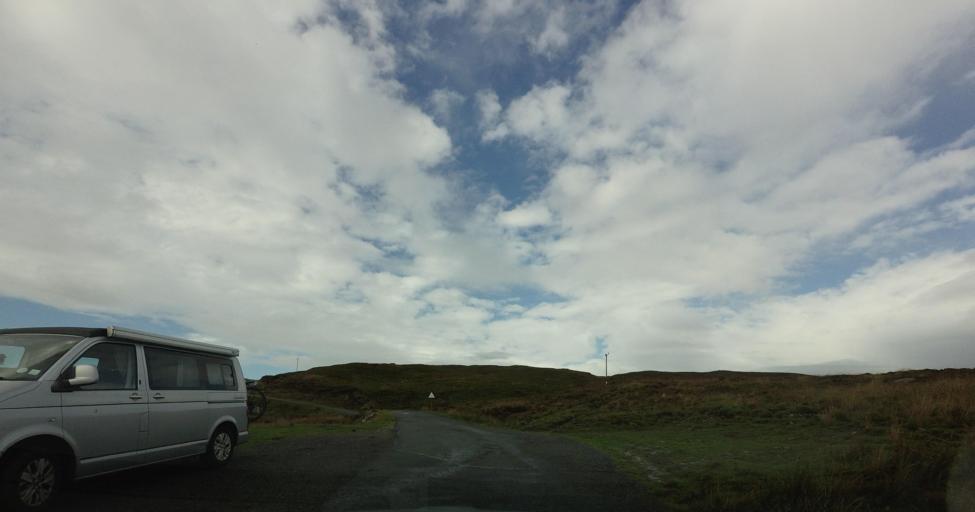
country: GB
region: Scotland
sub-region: Highland
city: Isle of Skye
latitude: 57.1423
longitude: -6.0727
